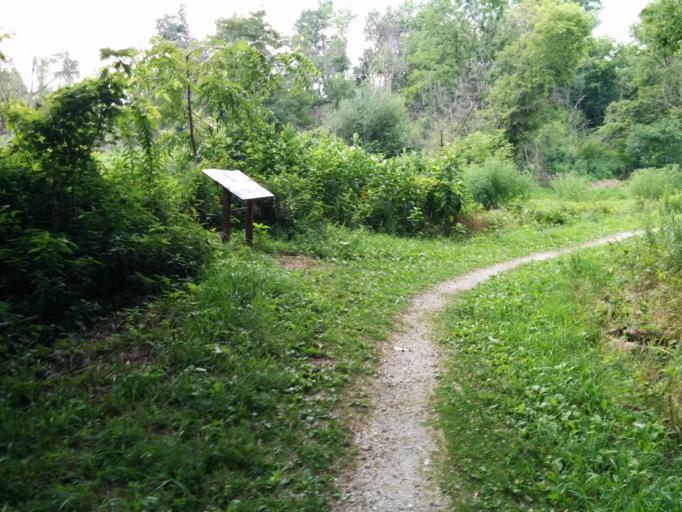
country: US
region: Illinois
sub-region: Cook County
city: Lyons
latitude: 41.8043
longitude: -87.8055
